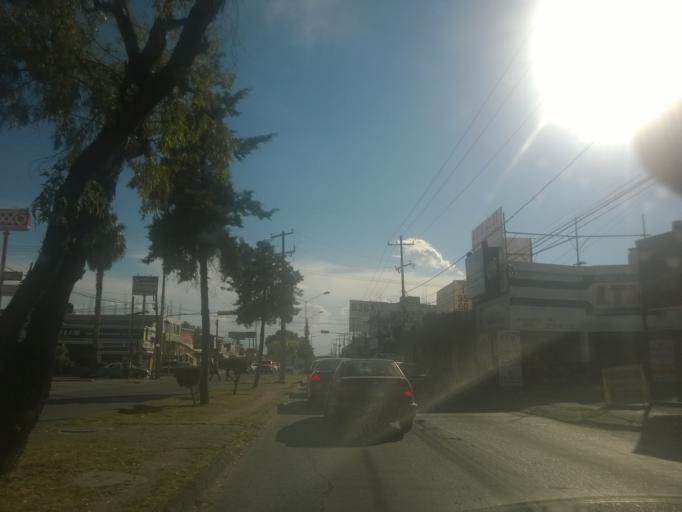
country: MX
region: Guanajuato
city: Leon
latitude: 21.1357
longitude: -101.6582
